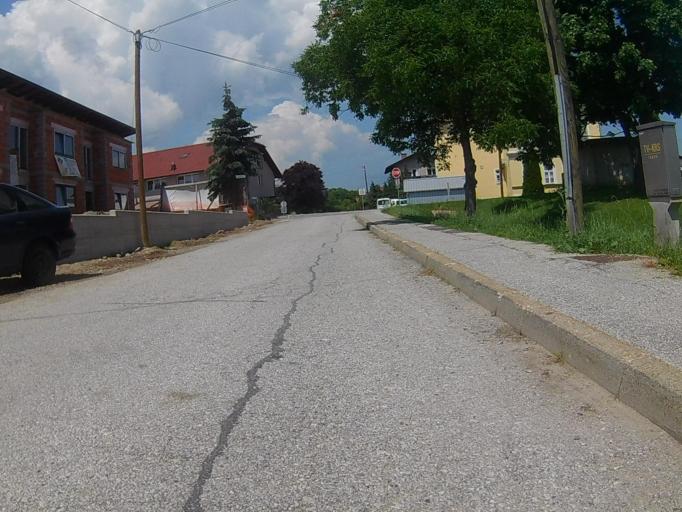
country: SI
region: Hoce-Slivnica
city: Spodnje Hoce
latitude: 46.4985
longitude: 15.6460
